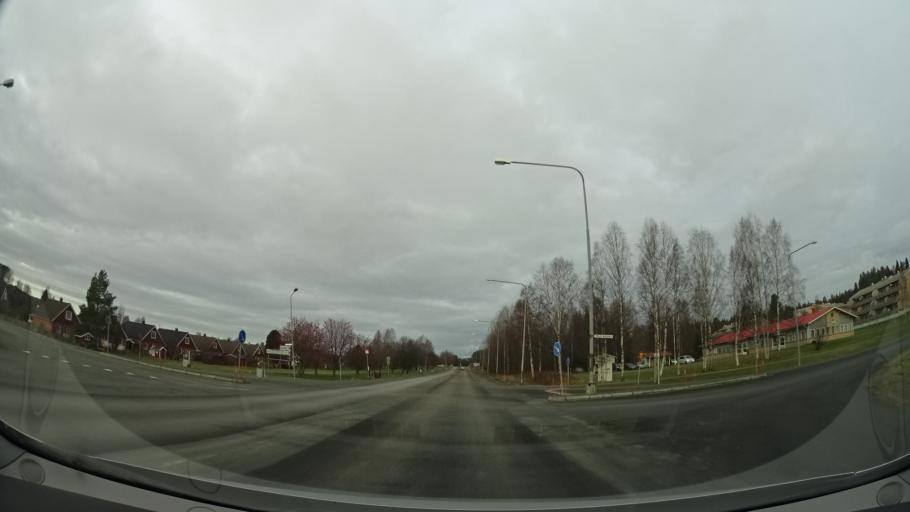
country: SE
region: Vaesterbotten
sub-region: Skelleftea Kommun
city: Skelleftea
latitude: 64.7493
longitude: 21.0253
